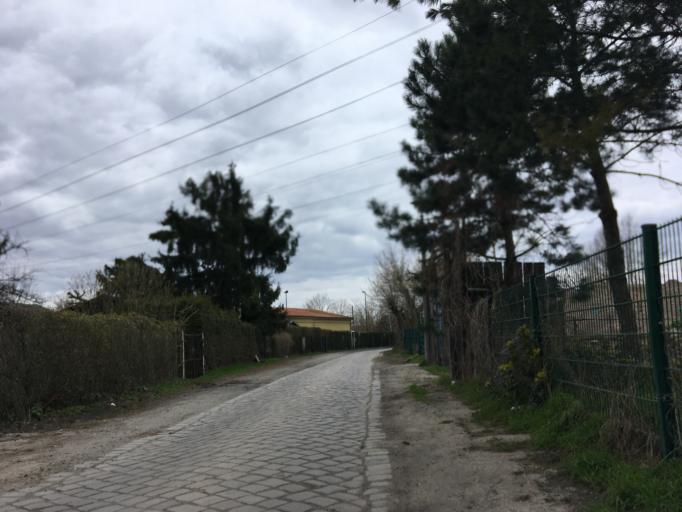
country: DE
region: Berlin
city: Oberschoneweide
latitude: 52.4796
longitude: 13.5103
